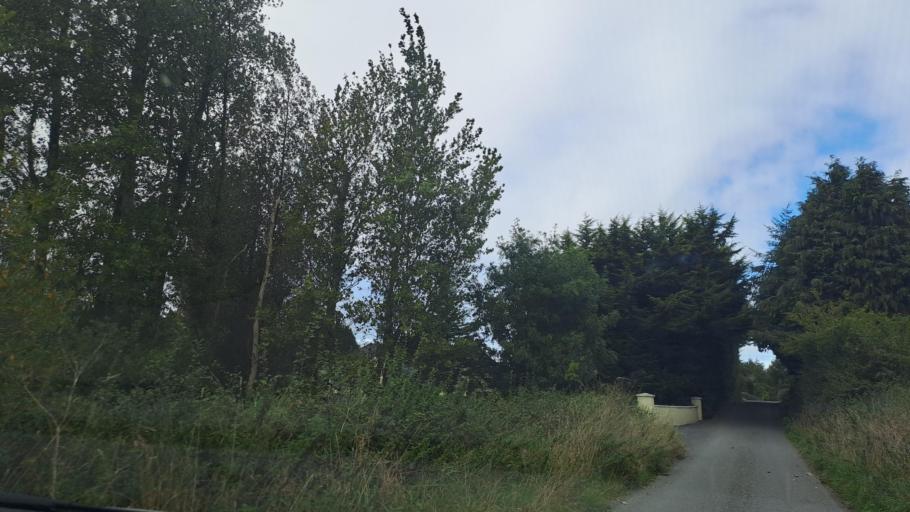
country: IE
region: Ulster
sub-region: An Cabhan
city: Kingscourt
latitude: 53.9889
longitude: -6.7992
